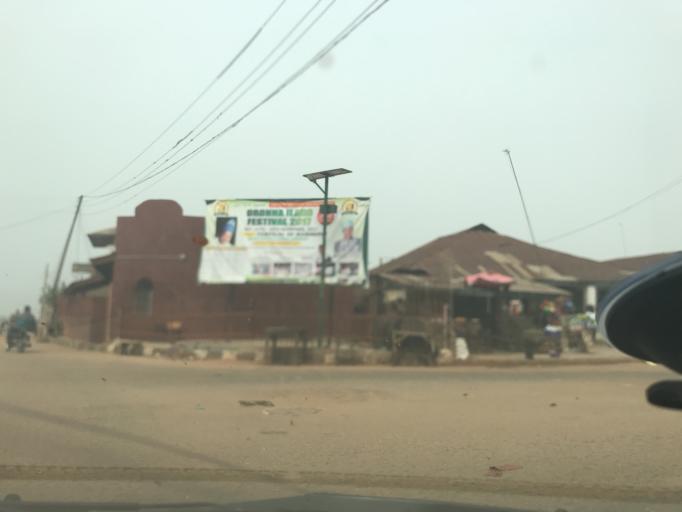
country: NG
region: Ogun
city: Ilaro
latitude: 6.8903
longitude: 3.0154
